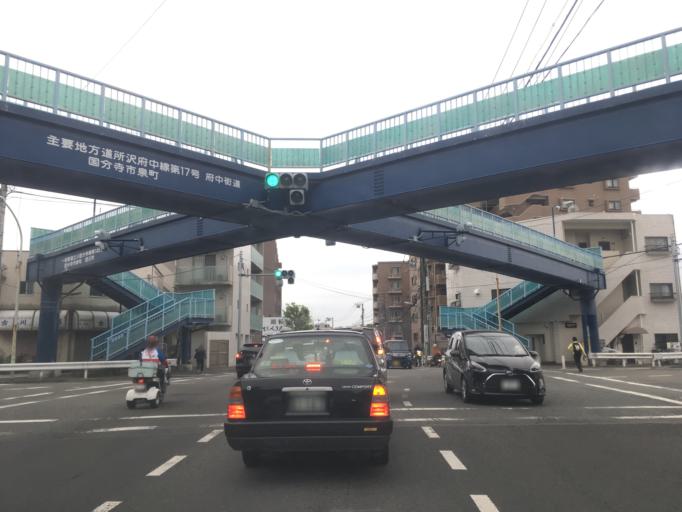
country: JP
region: Tokyo
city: Kokubunji
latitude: 35.6958
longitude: 139.4671
